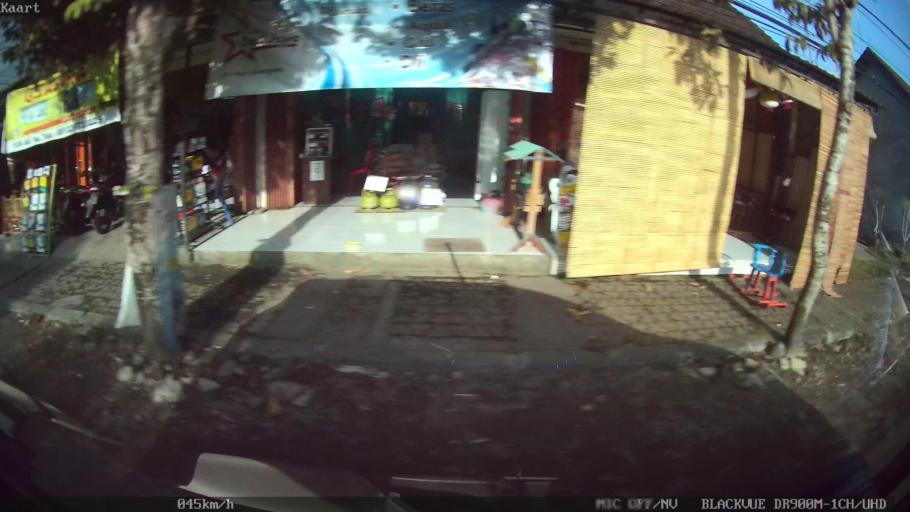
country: ID
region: Bali
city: Banjar Parekan
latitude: -8.5769
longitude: 115.2178
